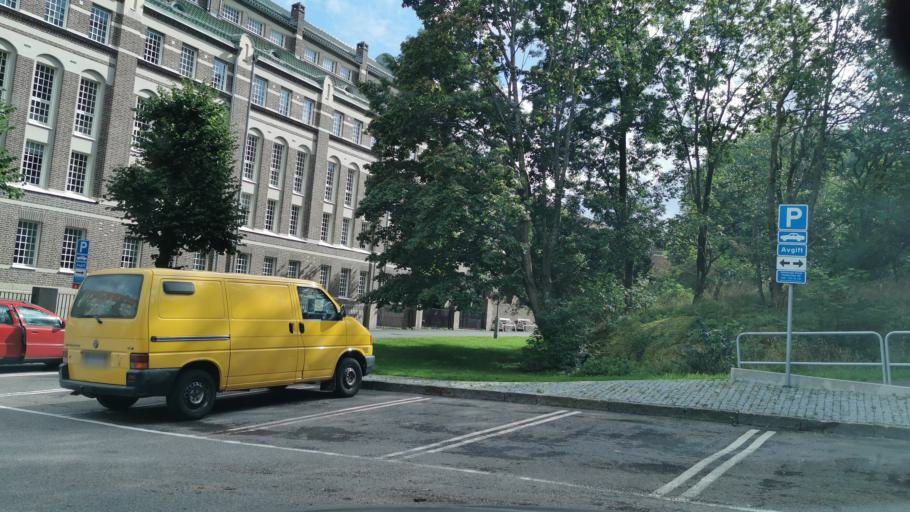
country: SE
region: Vaestra Goetaland
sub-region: Goteborg
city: Goeteborg
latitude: 57.6969
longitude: 11.9752
